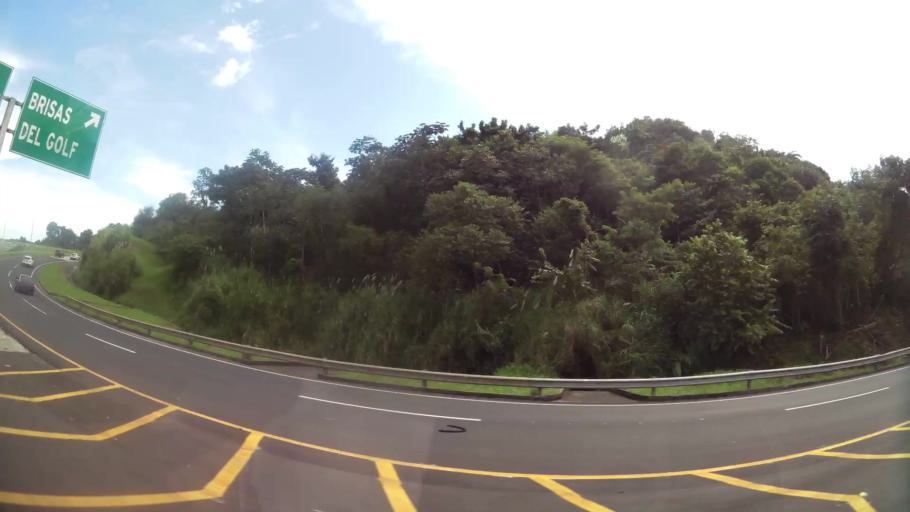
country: PA
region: Panama
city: San Miguelito
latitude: 9.0826
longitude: -79.4627
